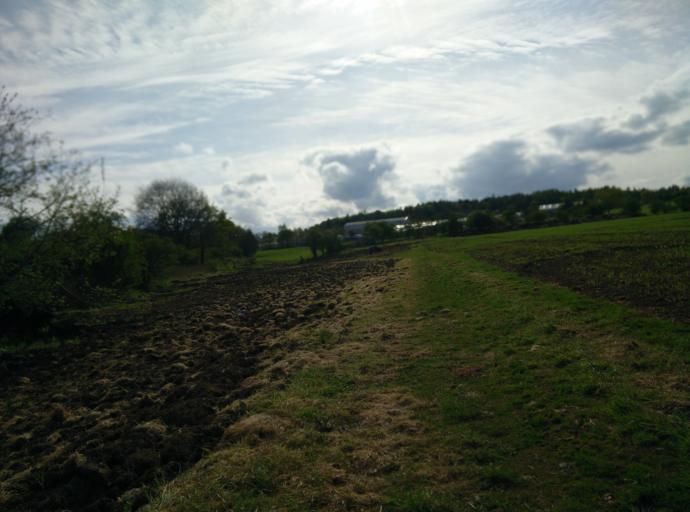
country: GB
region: Scotland
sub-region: Midlothian
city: Loanhead
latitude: 55.8835
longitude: -3.1369
